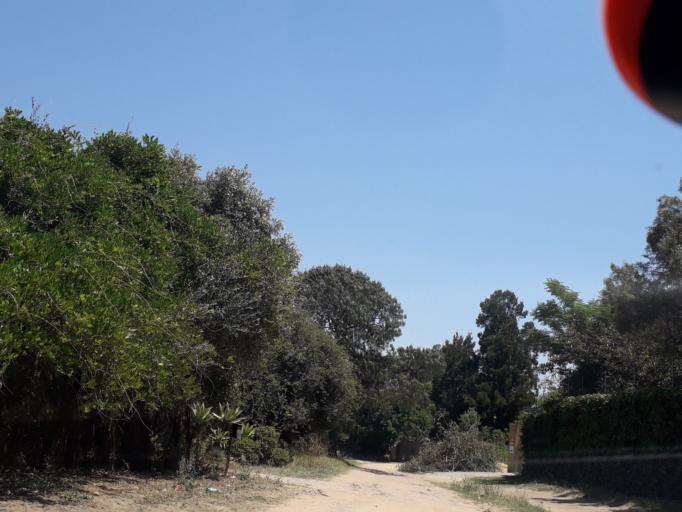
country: ZA
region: Gauteng
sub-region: City of Johannesburg Metropolitan Municipality
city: Midrand
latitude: -26.0209
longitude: 28.1309
